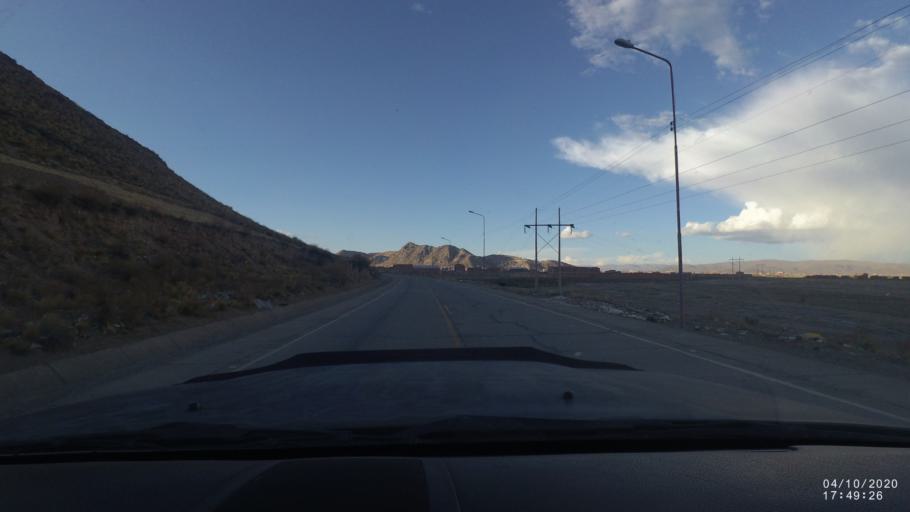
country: BO
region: Oruro
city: Oruro
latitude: -18.0114
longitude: -67.1368
